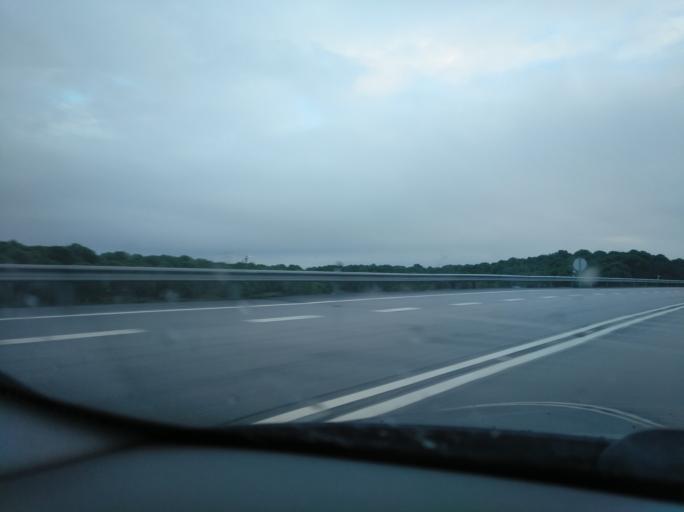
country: PT
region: Faro
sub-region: Alcoutim
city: Alcoutim
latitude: 37.4220
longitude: -7.5236
